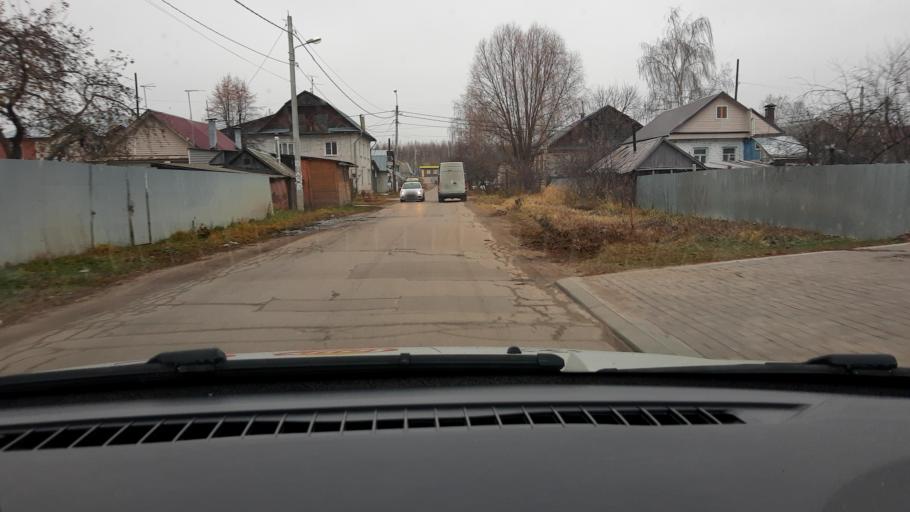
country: RU
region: Nizjnij Novgorod
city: Burevestnik
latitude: 56.2038
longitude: 43.7785
